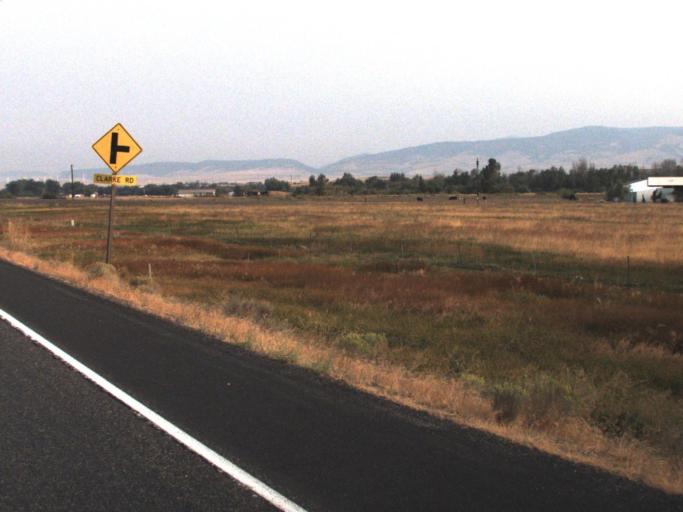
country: US
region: Washington
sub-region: Kittitas County
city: Ellensburg
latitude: 47.0555
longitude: -120.6162
